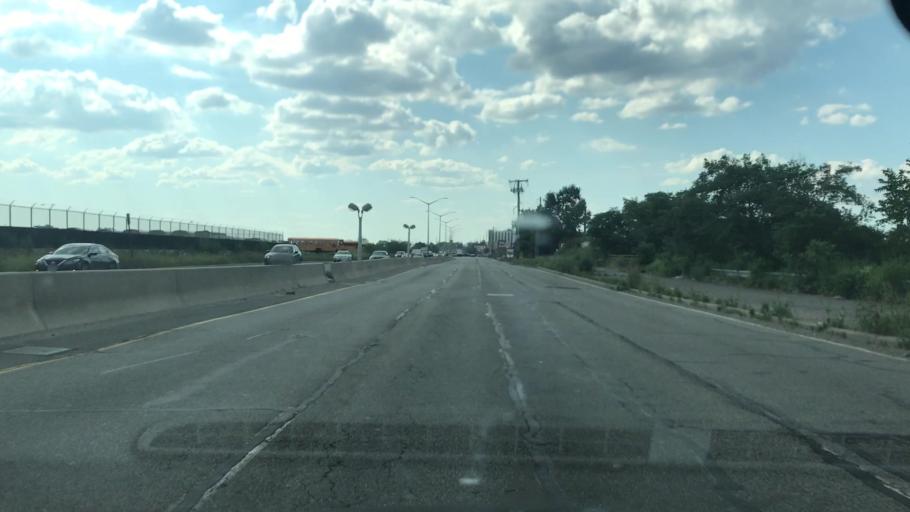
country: US
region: New York
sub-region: Nassau County
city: Inwood
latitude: 40.6538
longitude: -73.7629
